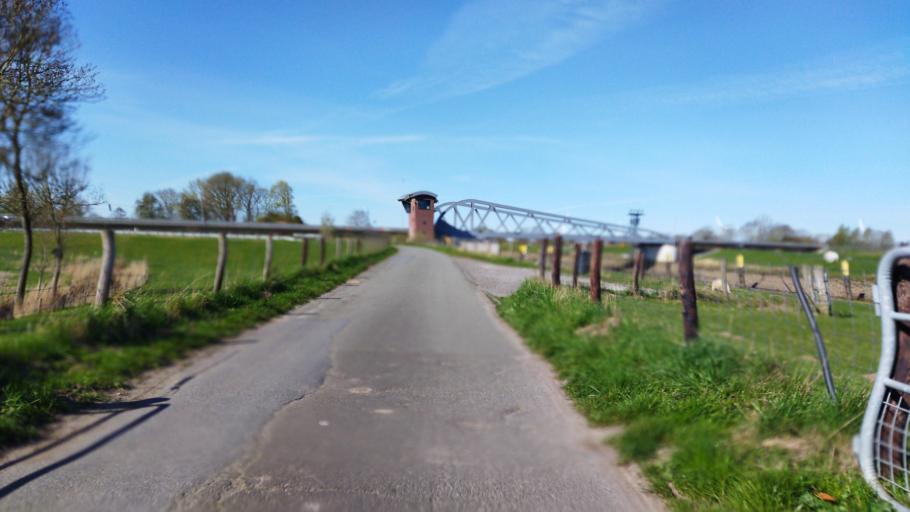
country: DE
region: Lower Saxony
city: Elsfleth
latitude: 53.2001
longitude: 8.4505
